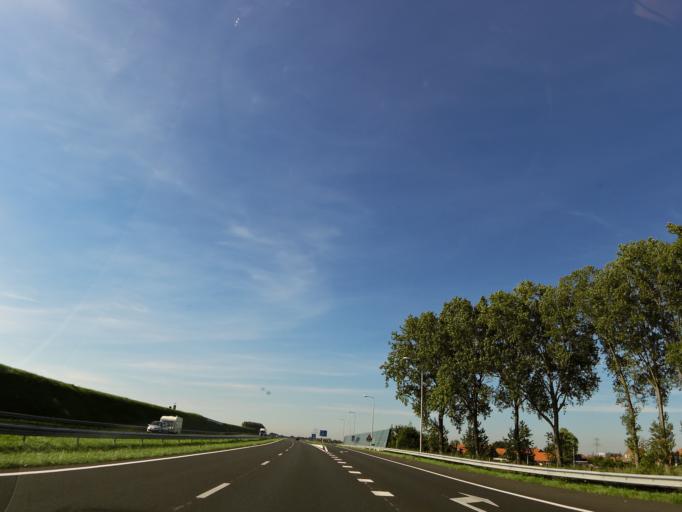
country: NL
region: Zeeland
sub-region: Gemeente Middelburg
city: Middelburg
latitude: 51.4846
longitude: 3.6560
